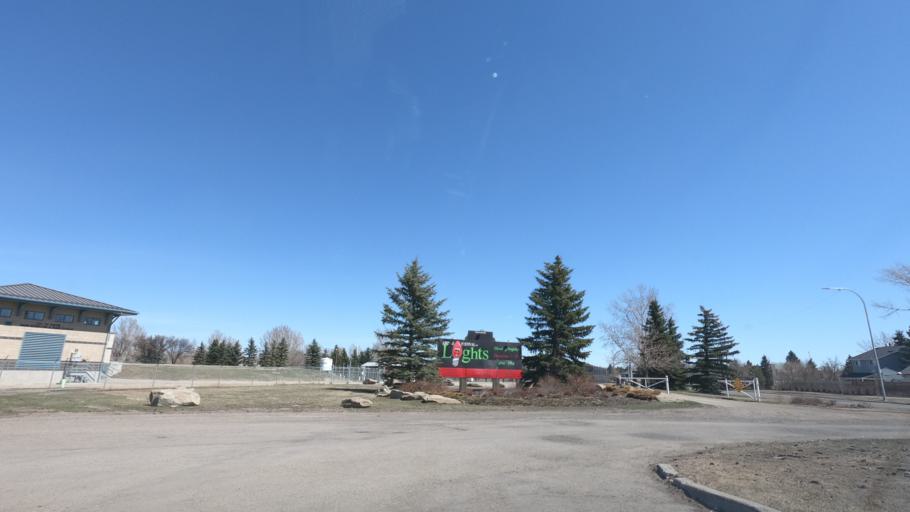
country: CA
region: Alberta
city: Airdrie
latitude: 51.2780
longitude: -114.0126
